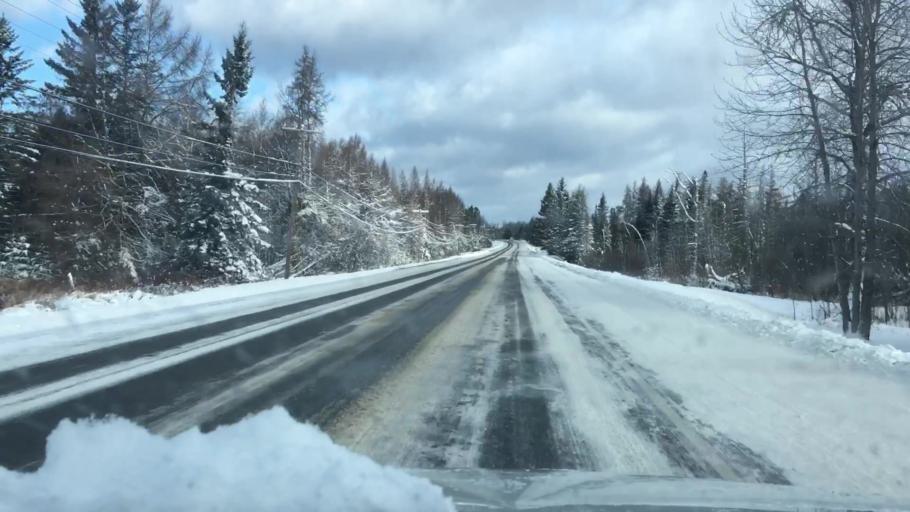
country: US
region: Maine
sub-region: Aroostook County
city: Caribou
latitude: 46.9194
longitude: -68.0191
